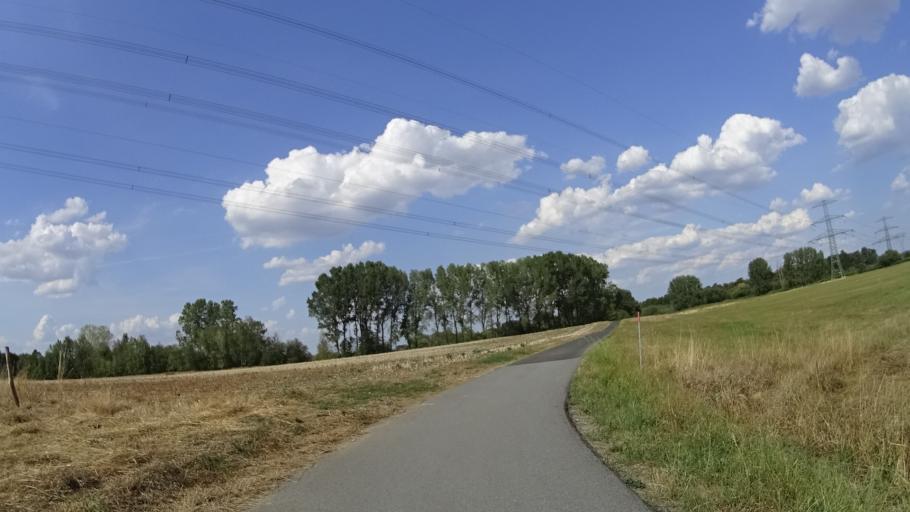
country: DE
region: Saxony
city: Ostritz
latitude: 51.0510
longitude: 14.9579
